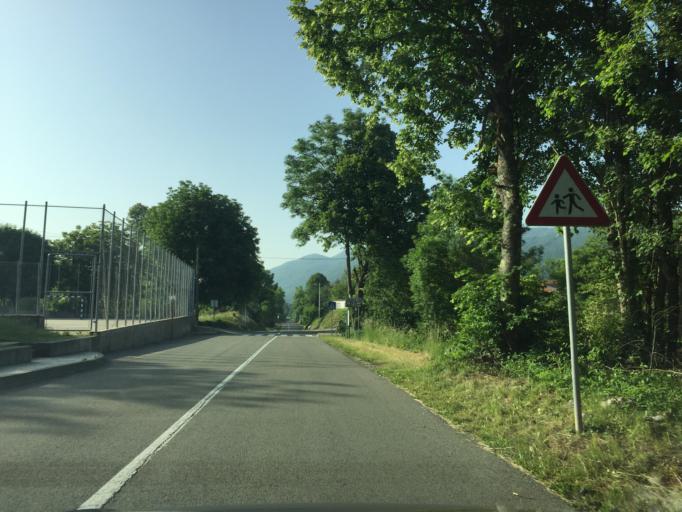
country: HR
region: Primorsko-Goranska
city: Matulji
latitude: 45.4423
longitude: 14.1941
